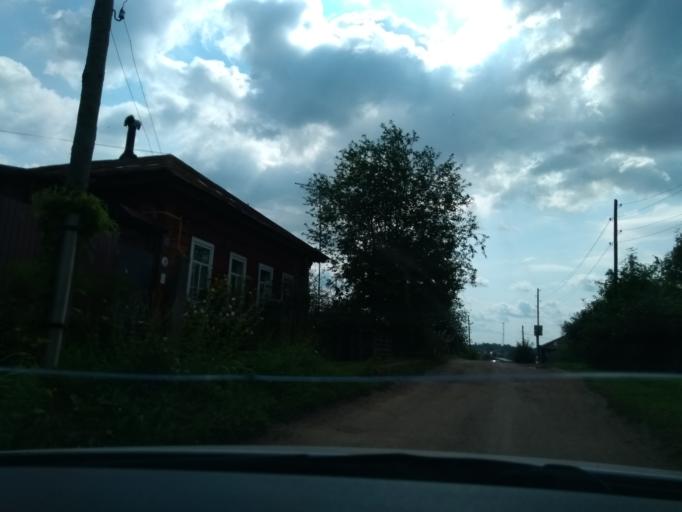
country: RU
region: Perm
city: Lobanovo
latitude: 57.8665
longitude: 56.3061
